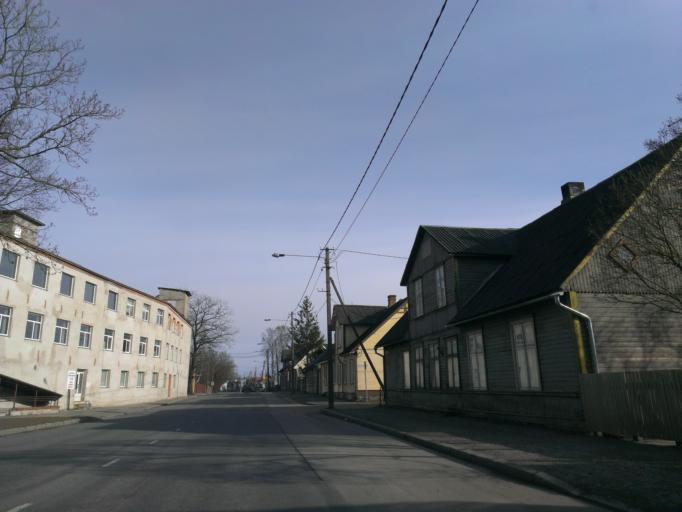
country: EE
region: Paernumaa
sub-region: Paernu linn
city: Parnu
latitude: 58.3889
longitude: 24.4744
